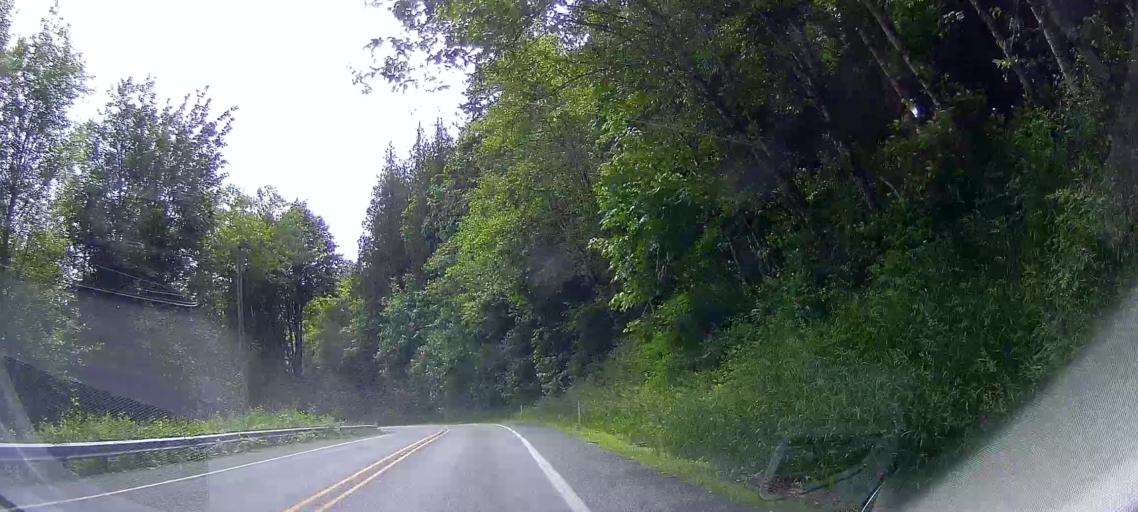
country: US
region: Washington
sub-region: Whatcom County
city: Sudden Valley
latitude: 48.7071
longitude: -122.2027
